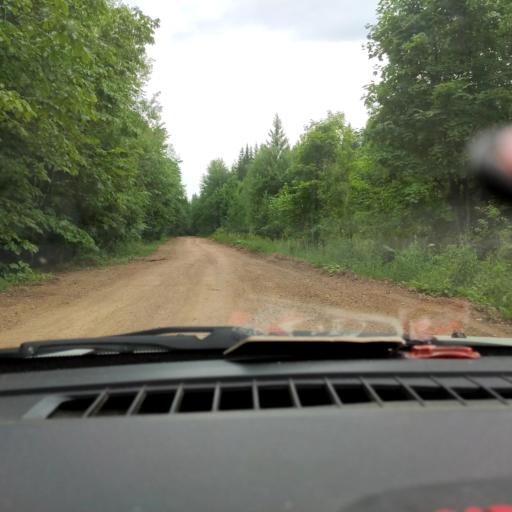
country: RU
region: Perm
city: Kultayevo
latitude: 57.8105
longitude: 56.0043
